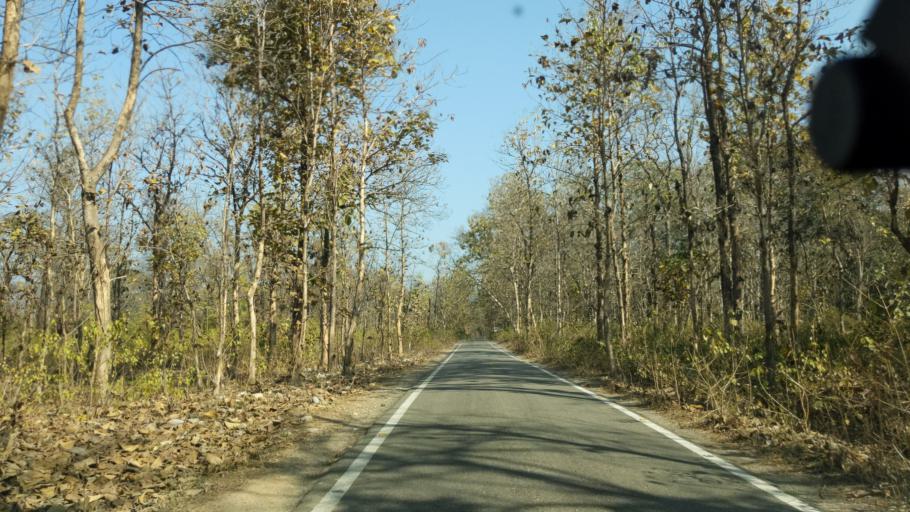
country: IN
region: Uttarakhand
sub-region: Naini Tal
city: Ramnagar
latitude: 29.4279
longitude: 79.1401
